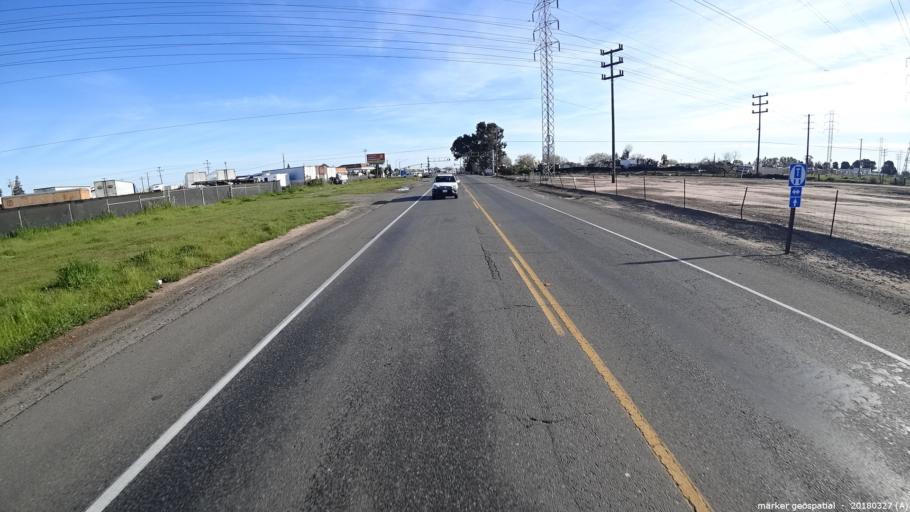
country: US
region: California
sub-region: Sacramento County
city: Florin
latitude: 38.5084
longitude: -121.3713
